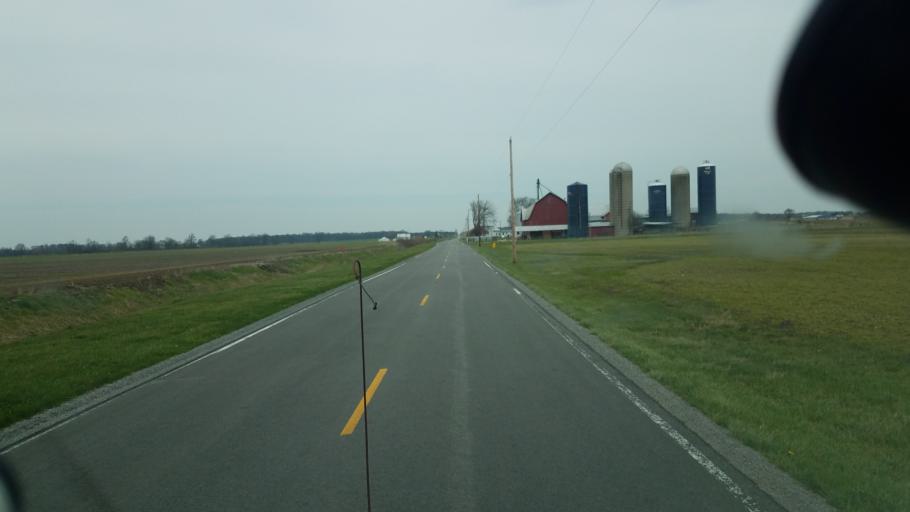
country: US
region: Ohio
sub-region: Wyandot County
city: Carey
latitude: 41.0223
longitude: -83.4775
